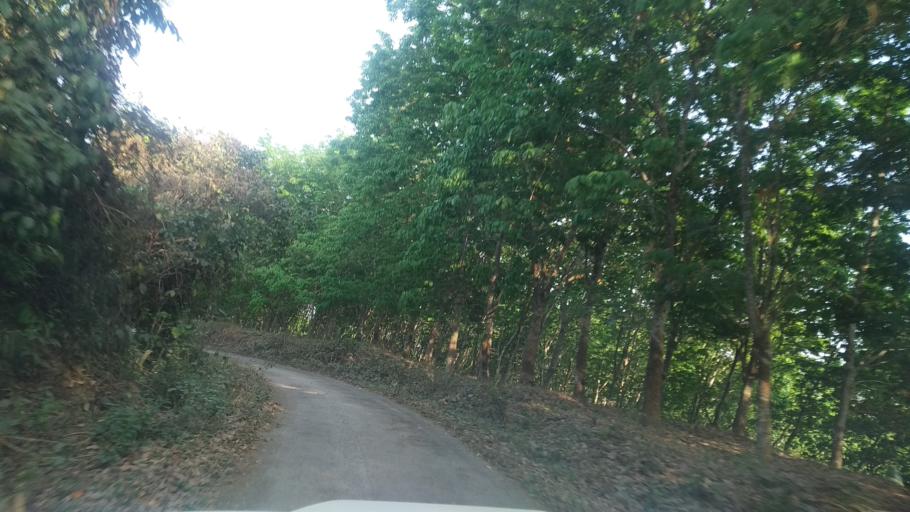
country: IN
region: Tripura
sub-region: West Tripura
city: Sonamura
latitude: 23.4439
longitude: 91.3662
